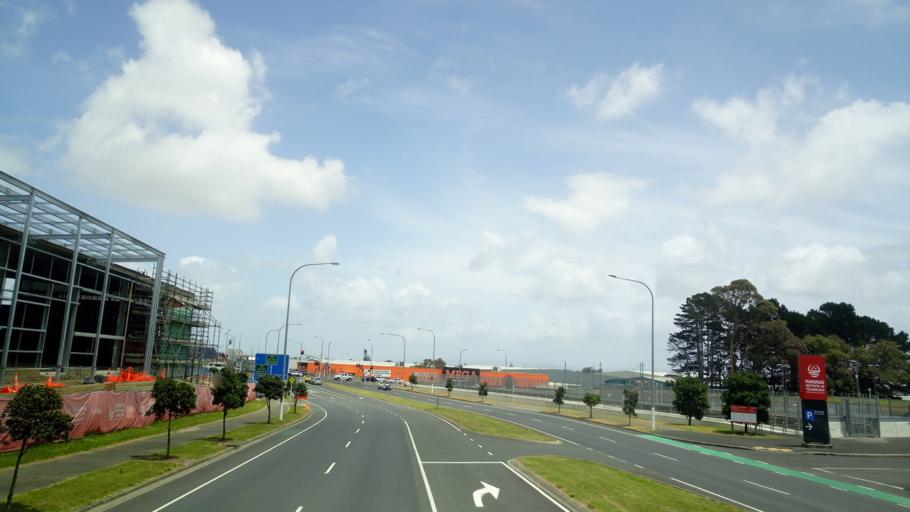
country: NZ
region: Auckland
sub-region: Auckland
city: Manukau City
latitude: -36.9948
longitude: 174.8764
